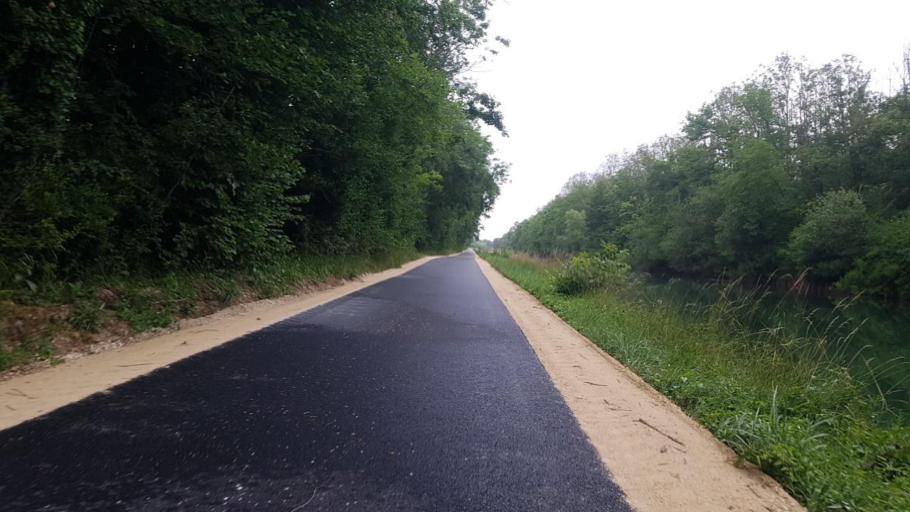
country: FR
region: Champagne-Ardenne
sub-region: Departement de la Marne
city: Vitry-le-Francois
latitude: 48.8024
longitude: 4.5232
